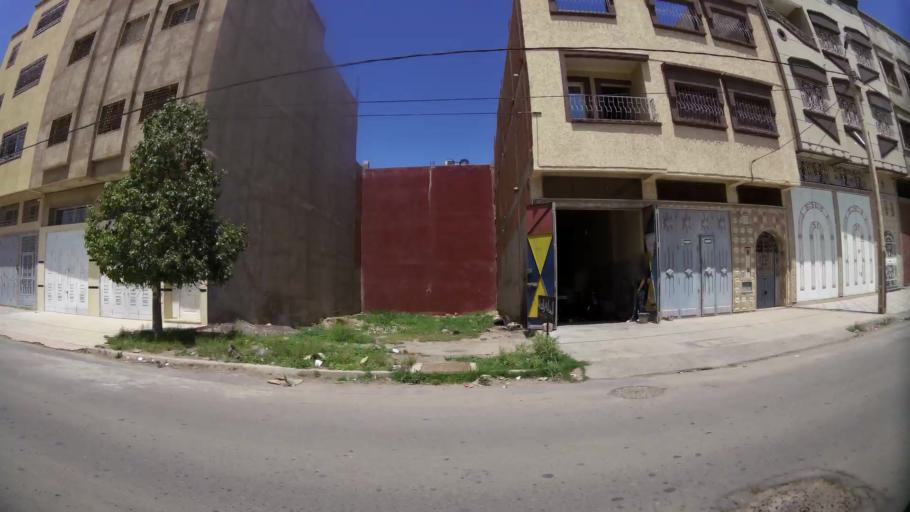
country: MA
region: Oriental
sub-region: Oujda-Angad
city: Oujda
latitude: 34.6931
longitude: -1.8911
